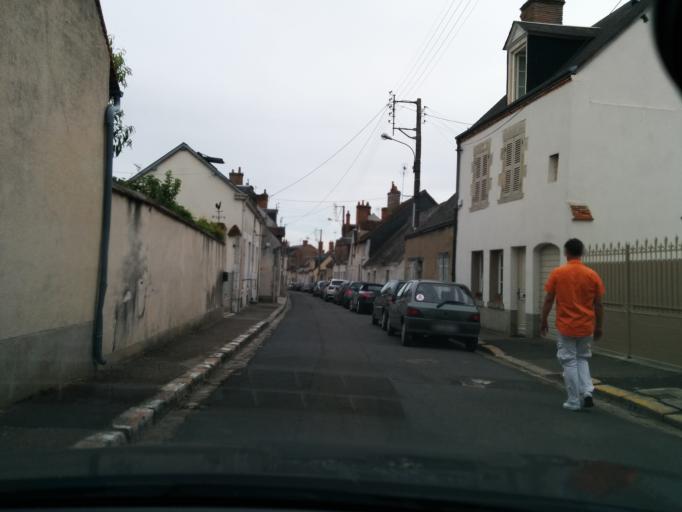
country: FR
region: Centre
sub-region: Departement du Loiret
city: Chateauneuf-sur-Loire
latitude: 47.8616
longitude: 2.2213
